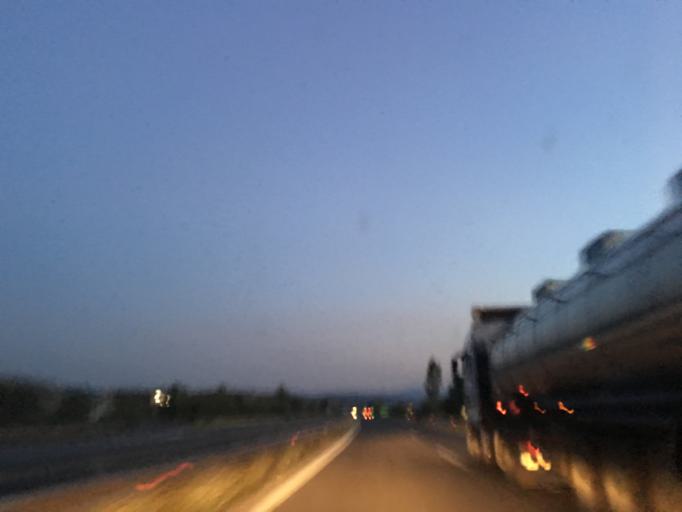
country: MK
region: Petrovec
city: Petrovec
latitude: 41.9550
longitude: 21.6307
